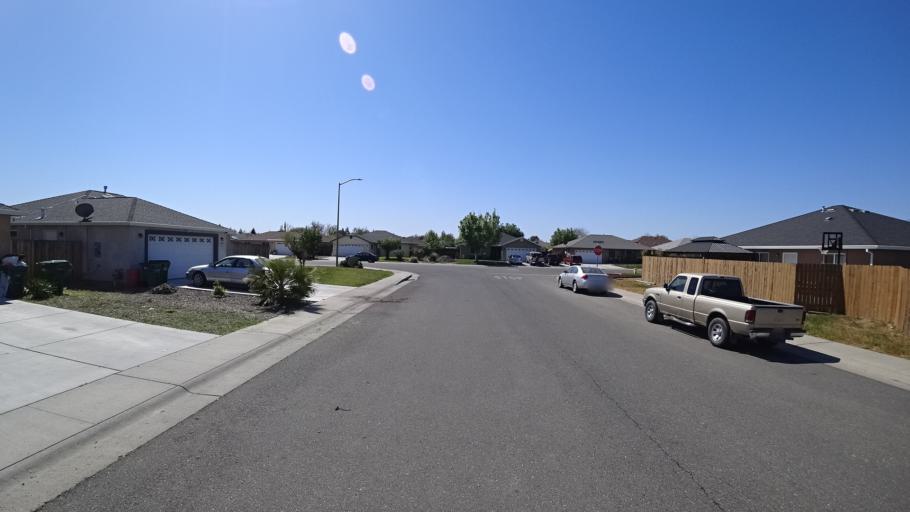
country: US
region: California
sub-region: Glenn County
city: Orland
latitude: 39.7602
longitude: -122.1999
